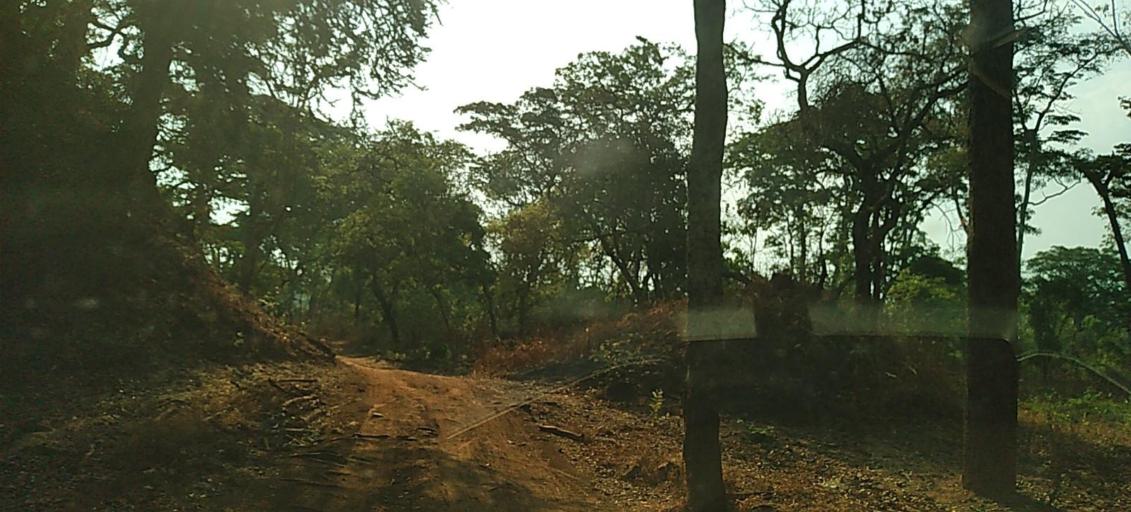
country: ZM
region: North-Western
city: Solwezi
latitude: -12.0594
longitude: 26.1667
